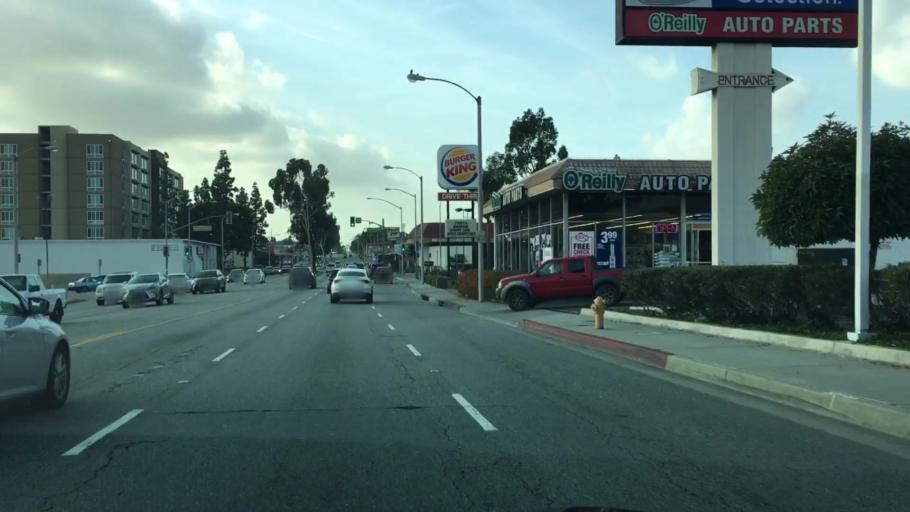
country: US
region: California
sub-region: Los Angeles County
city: Montebello
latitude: 34.0183
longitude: -118.1109
